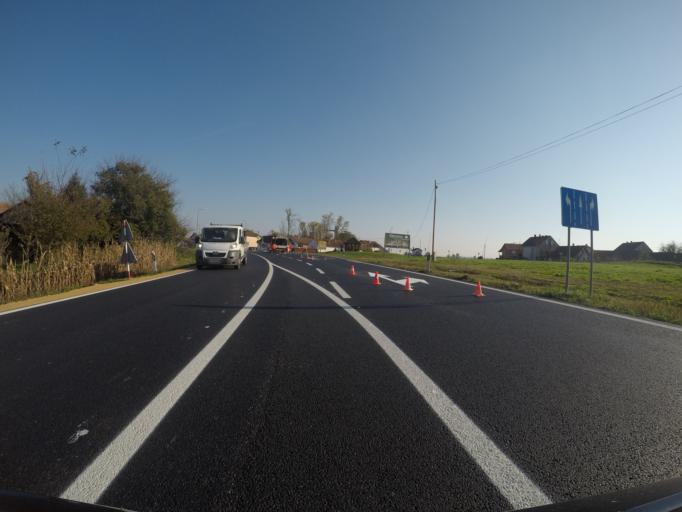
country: HR
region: Koprivnicko-Krizevacka
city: Kalinovac
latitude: 46.0306
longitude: 17.0627
